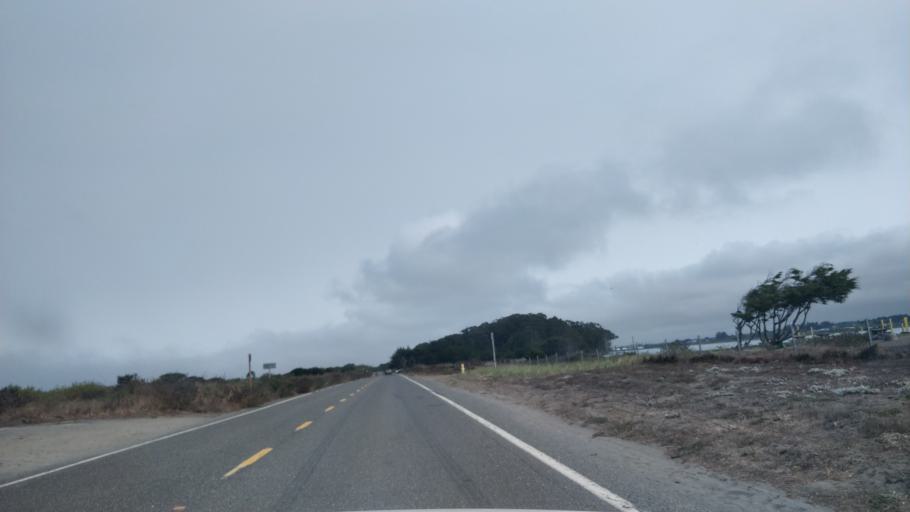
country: US
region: California
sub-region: Humboldt County
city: Bayview
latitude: 40.7726
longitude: -124.2137
